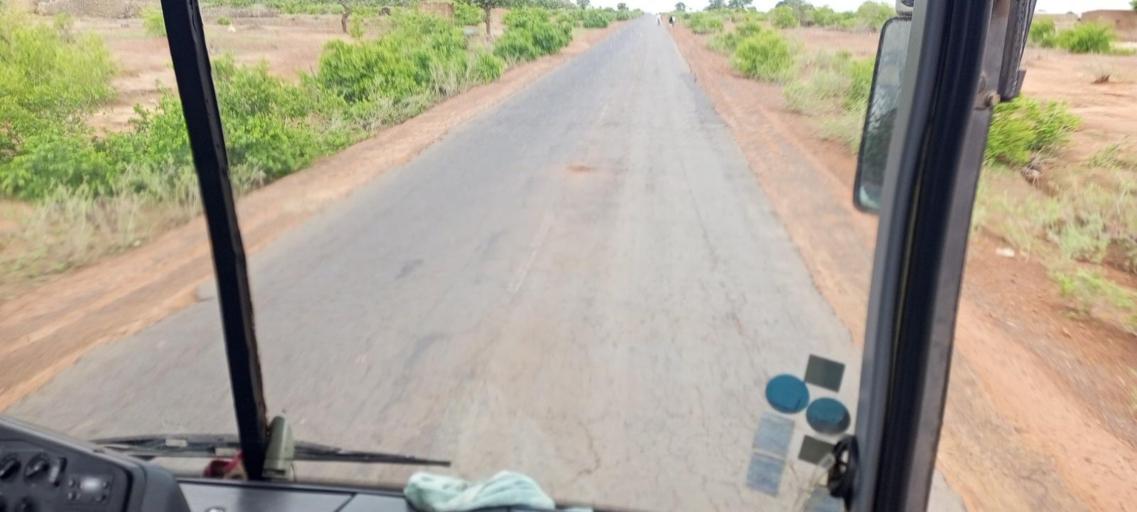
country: ML
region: Segou
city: Bla
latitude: 12.7199
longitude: -5.7249
